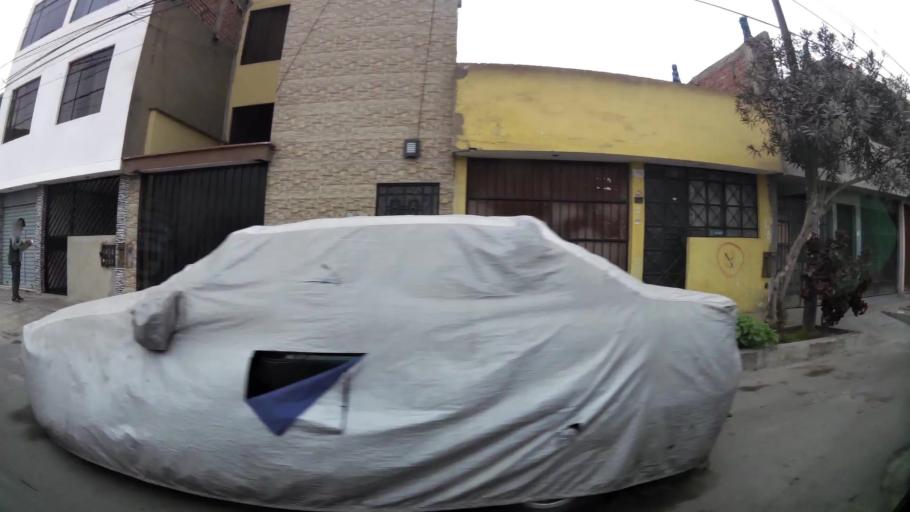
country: PE
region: Lima
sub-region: Lima
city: Independencia
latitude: -11.9692
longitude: -77.0734
